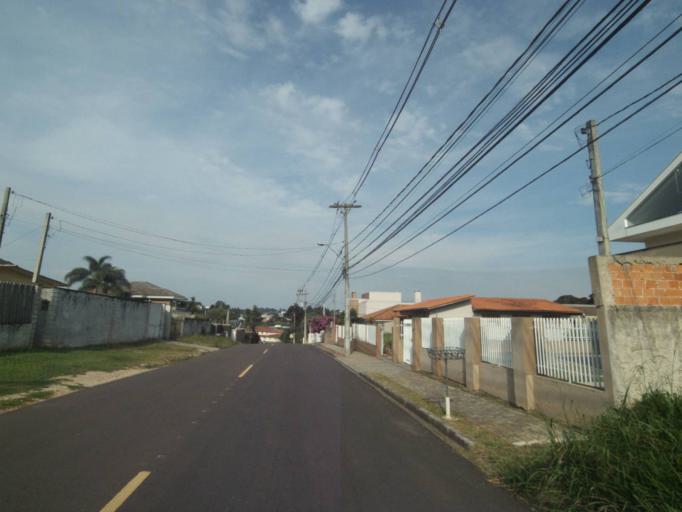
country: BR
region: Parana
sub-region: Curitiba
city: Curitiba
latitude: -25.4162
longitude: -49.3179
